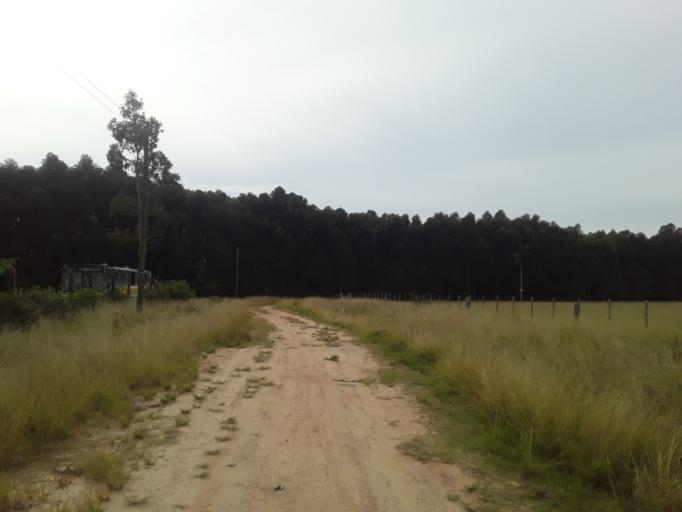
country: BR
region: Rio Grande do Sul
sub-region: Sao Lourenco Do Sul
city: Sao Lourenco do Sul
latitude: -31.3539
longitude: -51.9854
